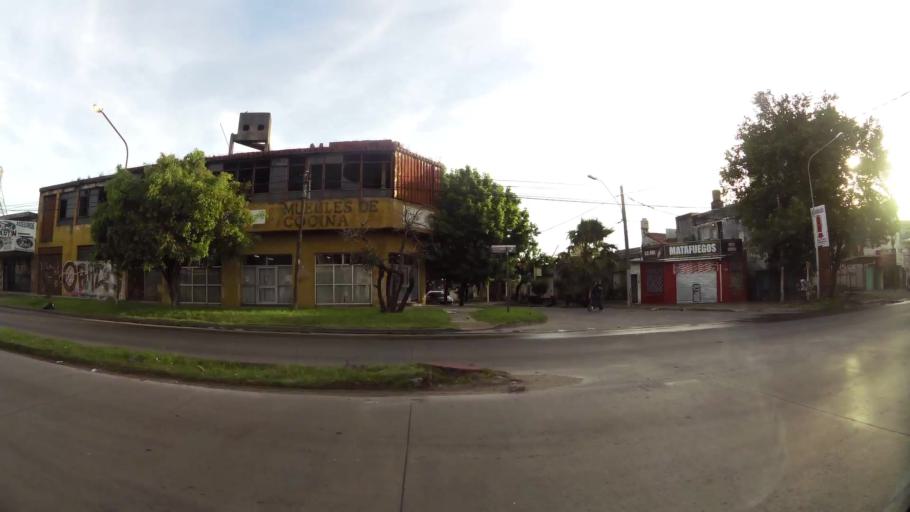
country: AR
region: Buenos Aires
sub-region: Partido de Moron
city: Moron
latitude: -34.6602
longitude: -58.6301
